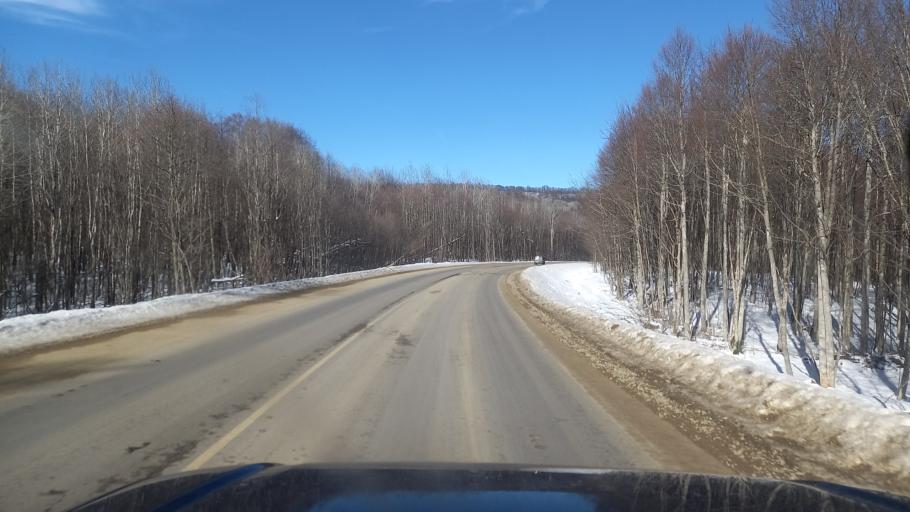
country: RU
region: Adygeya
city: Kamennomostskiy
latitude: 44.2122
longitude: 40.0769
